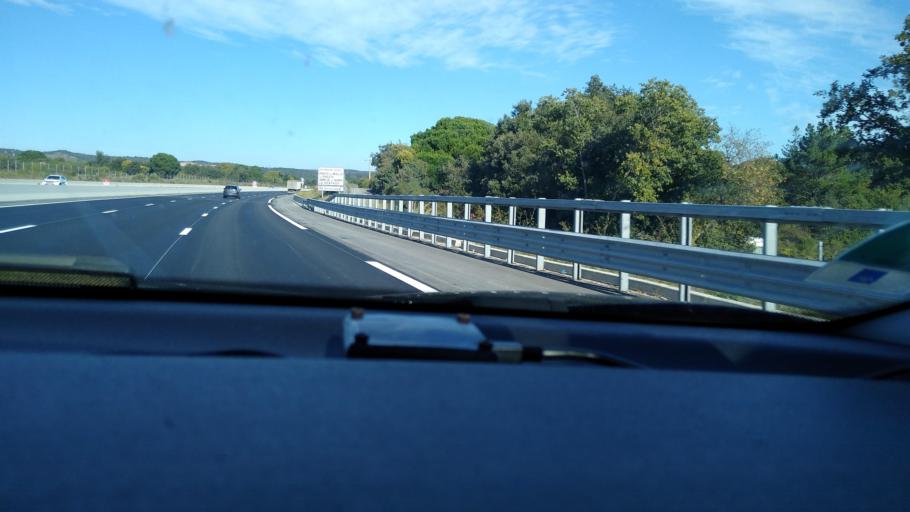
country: FR
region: Languedoc-Roussillon
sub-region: Departement des Pyrenees-Orientales
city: Maureillas-las-Illas
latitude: 42.5021
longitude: 2.8187
